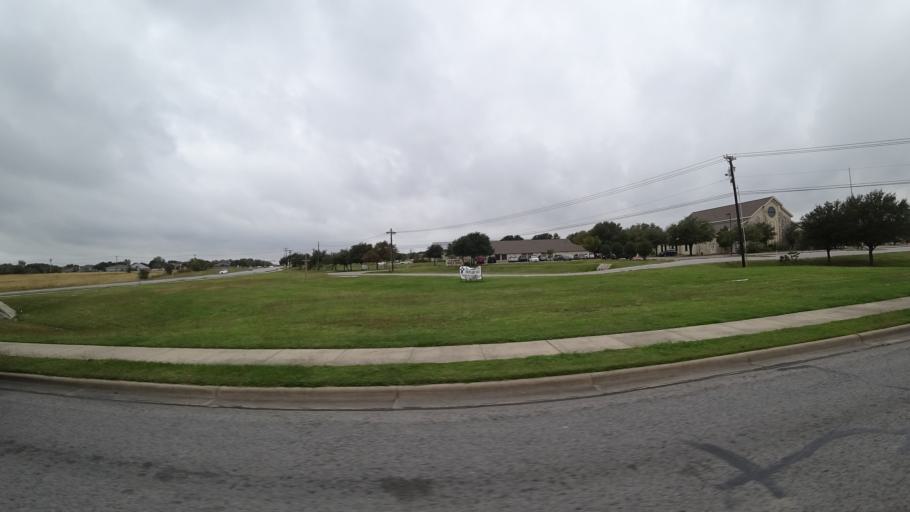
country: US
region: Texas
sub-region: Travis County
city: Pflugerville
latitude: 30.4594
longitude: -97.6167
